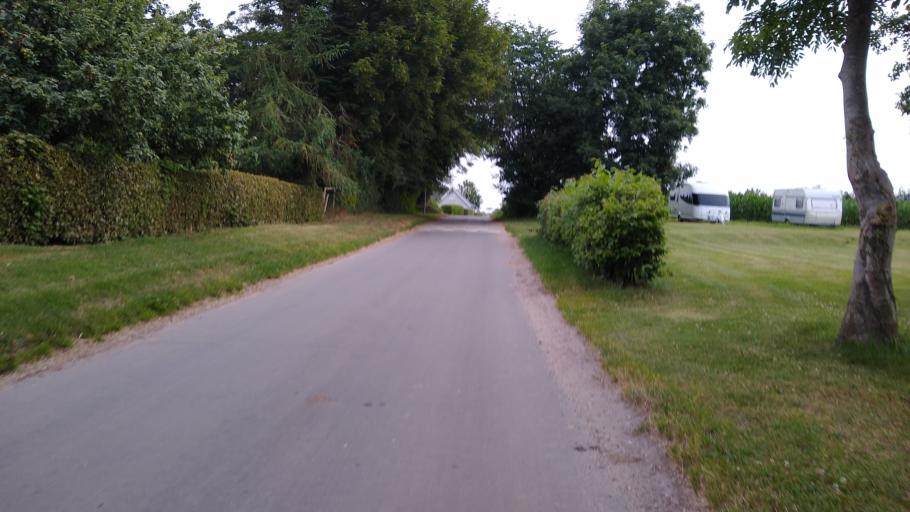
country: DK
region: South Denmark
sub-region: Vejle Kommune
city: Borkop
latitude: 55.6529
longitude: 9.6588
